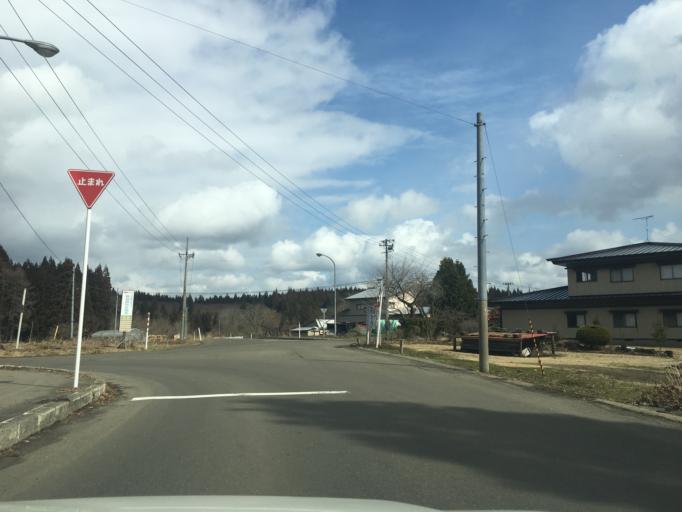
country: JP
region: Akita
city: Takanosu
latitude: 40.1875
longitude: 140.3419
